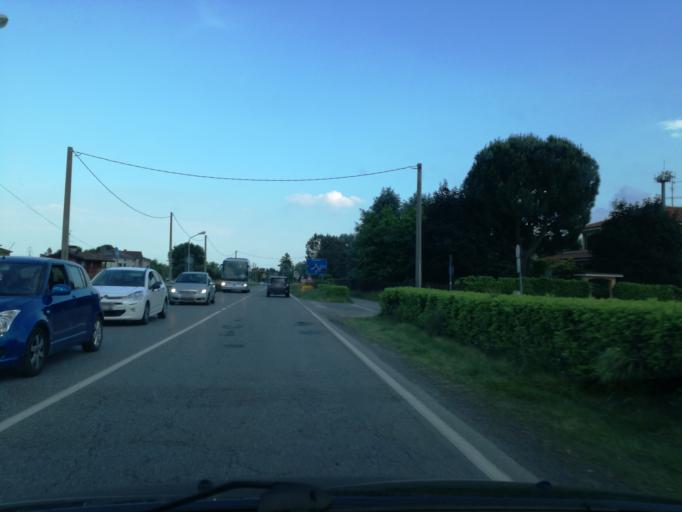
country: IT
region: Lombardy
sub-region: Provincia di Monza e Brianza
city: Cornate d'Adda
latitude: 45.6414
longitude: 9.4687
